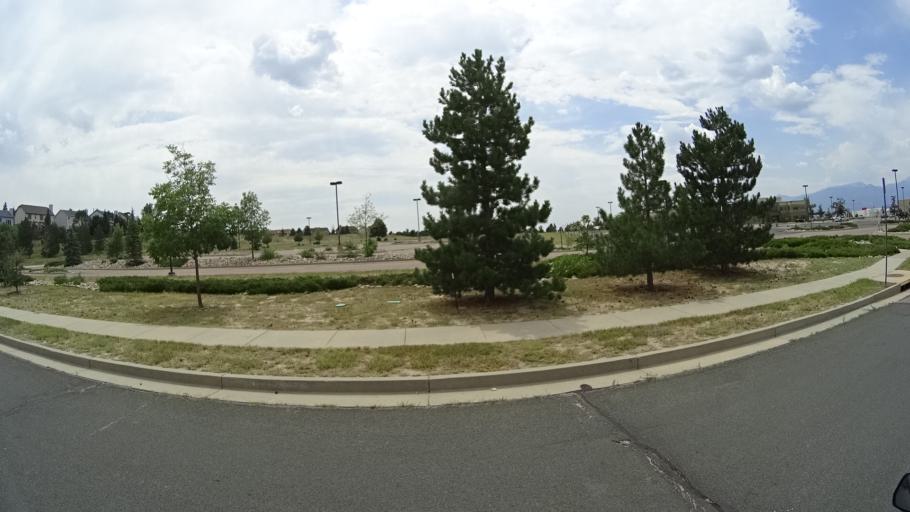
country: US
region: Colorado
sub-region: El Paso County
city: Air Force Academy
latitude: 38.9632
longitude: -104.7813
